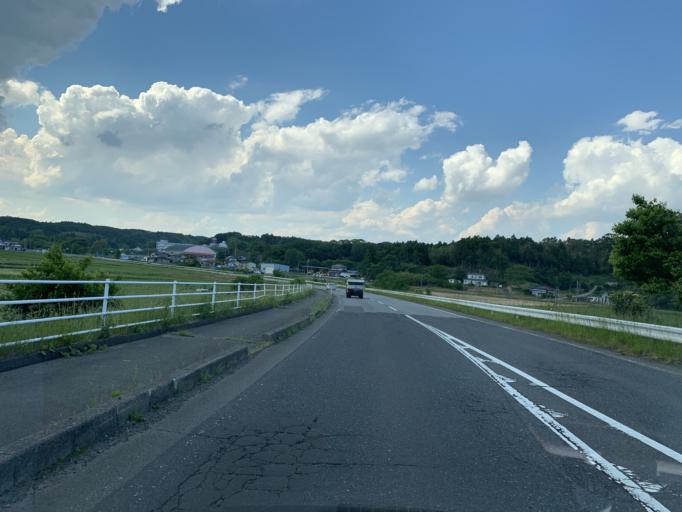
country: JP
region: Miyagi
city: Wakuya
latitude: 38.5409
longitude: 141.1496
